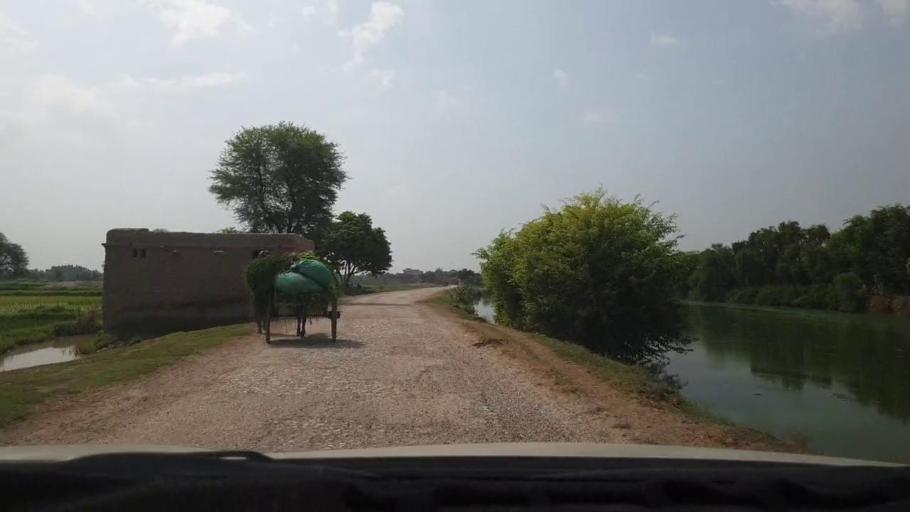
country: PK
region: Sindh
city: Dokri
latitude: 27.3835
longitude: 68.1249
